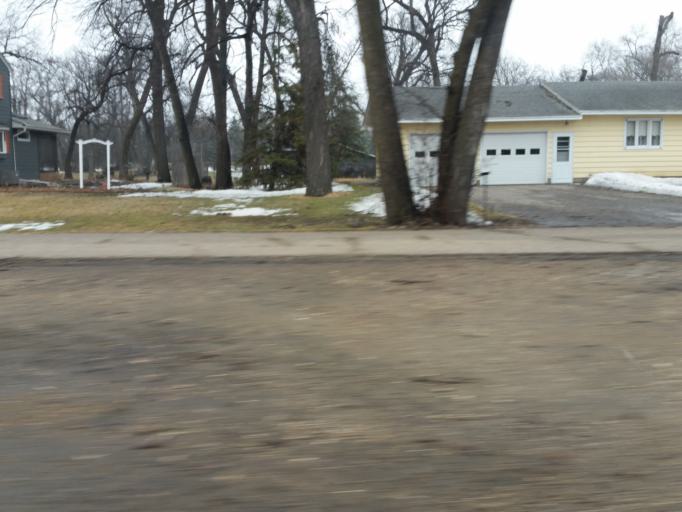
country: US
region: North Dakota
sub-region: Walsh County
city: Grafton
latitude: 48.4228
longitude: -97.3965
